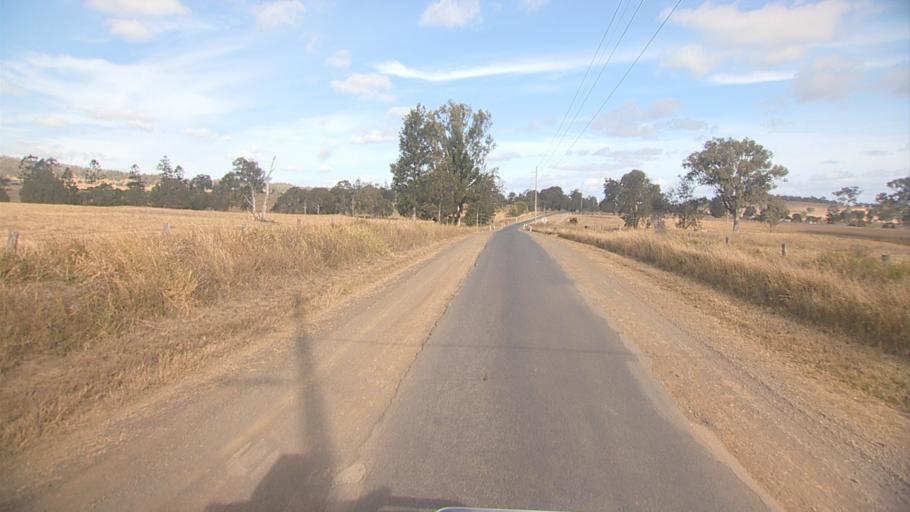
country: AU
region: Queensland
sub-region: Logan
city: Cedar Vale
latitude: -27.9135
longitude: 153.0137
